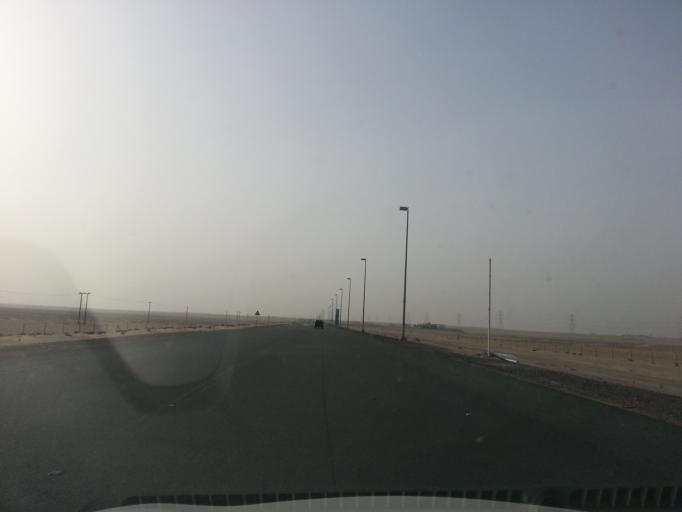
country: AE
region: Dubai
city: Dubai
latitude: 24.7974
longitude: 55.0735
